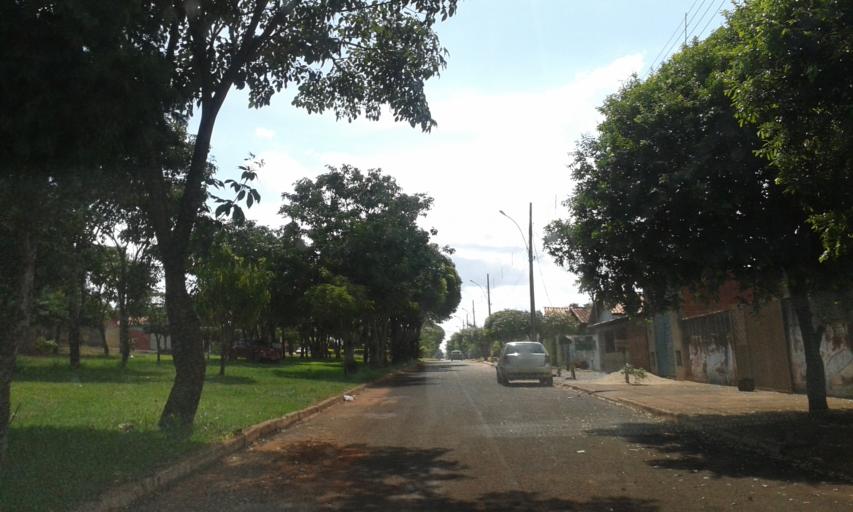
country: BR
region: Minas Gerais
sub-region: Santa Vitoria
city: Santa Vitoria
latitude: -18.8438
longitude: -50.1179
